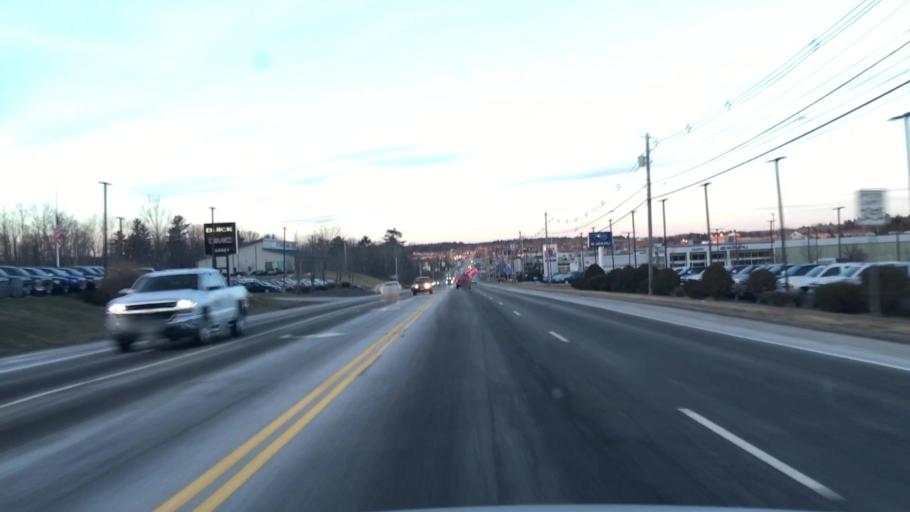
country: US
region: Maine
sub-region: Penobscot County
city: Brewer
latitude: 44.8229
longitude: -68.7397
